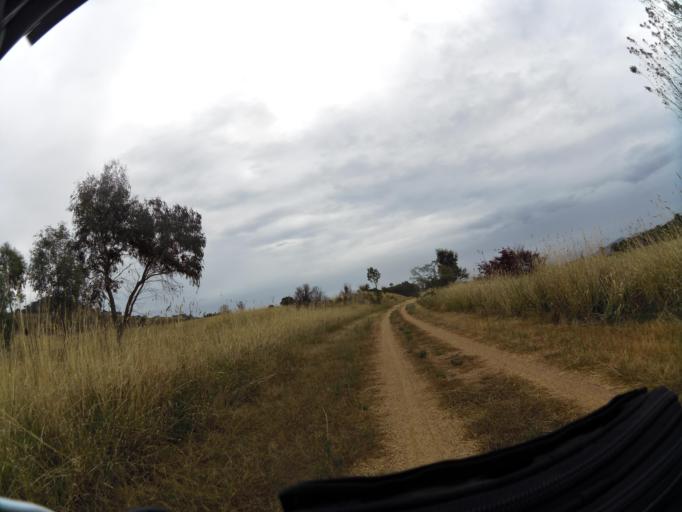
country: AU
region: New South Wales
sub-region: Albury Municipality
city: East Albury
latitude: -36.2155
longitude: 147.0576
